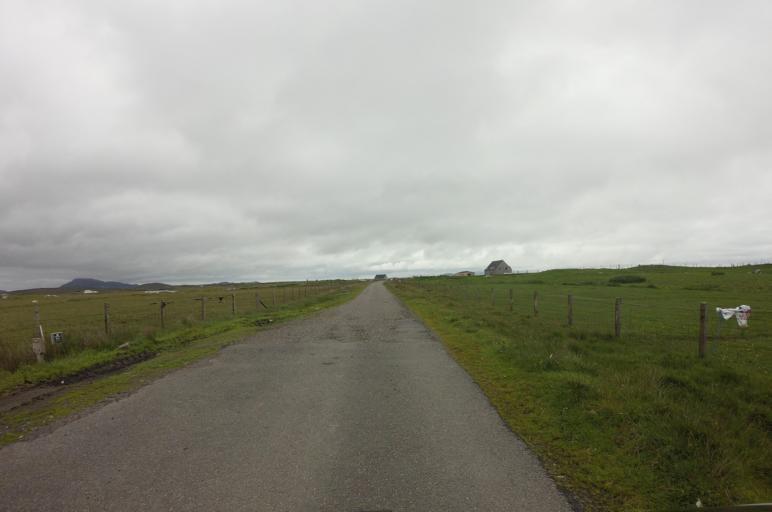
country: GB
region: Scotland
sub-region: Eilean Siar
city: Isle of North Uist
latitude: 57.5480
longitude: -7.3459
